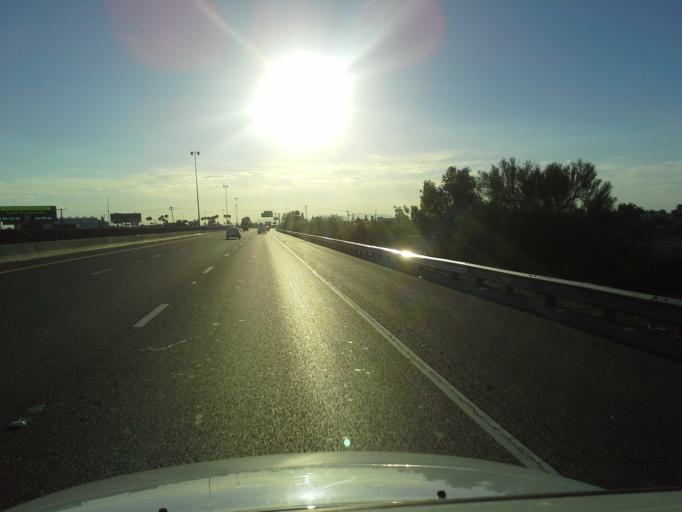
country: US
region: Arizona
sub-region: Maricopa County
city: Phoenix
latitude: 33.4285
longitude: -112.0574
